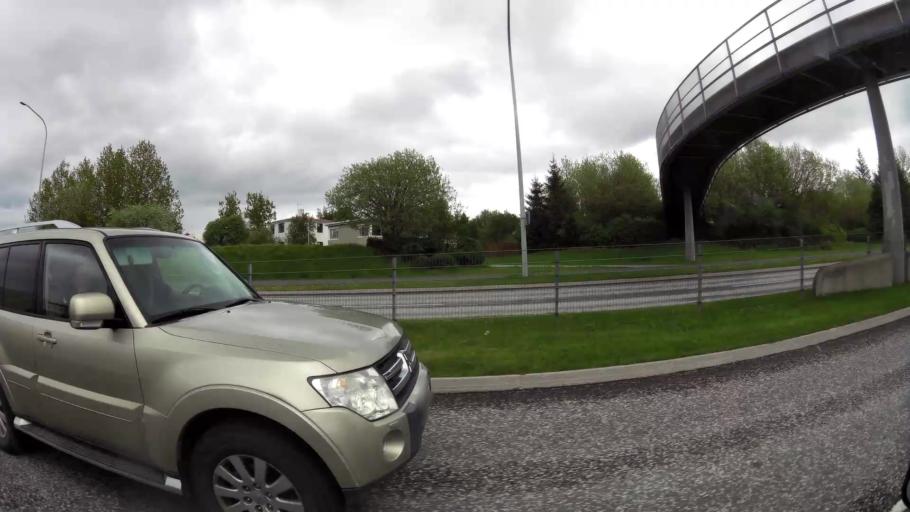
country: IS
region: Capital Region
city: Reykjavik
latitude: 64.1449
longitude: -21.8925
